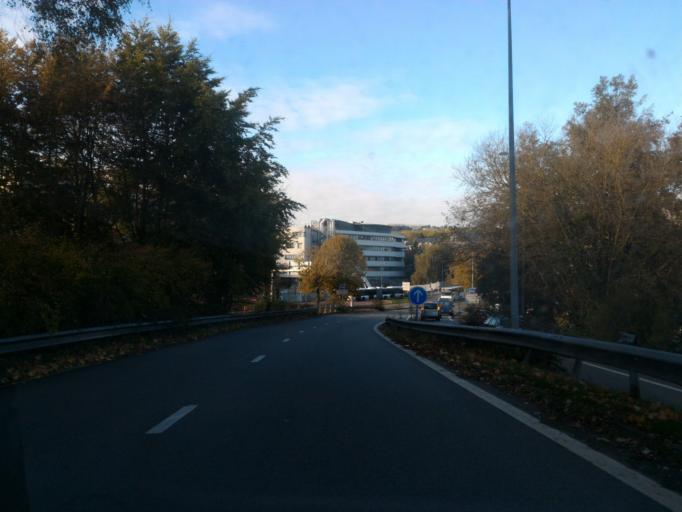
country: FR
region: Haute-Normandie
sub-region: Departement de la Seine-Maritime
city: Rouen
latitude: 49.4395
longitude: 1.1133
